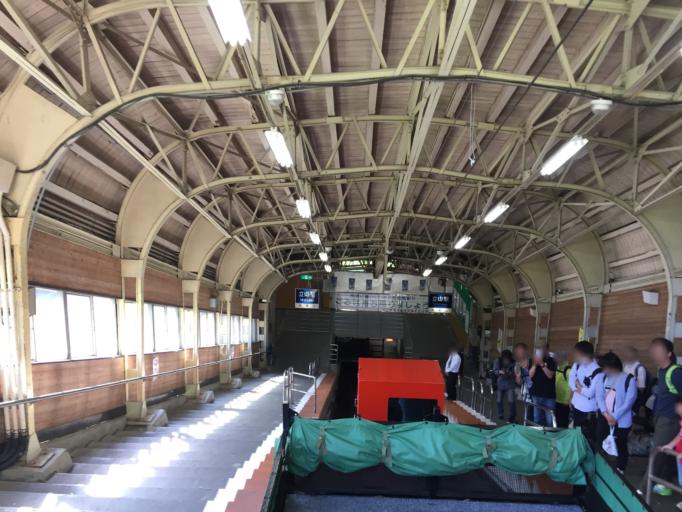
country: JP
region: Toyama
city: Kamiichi
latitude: 36.5833
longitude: 137.4458
